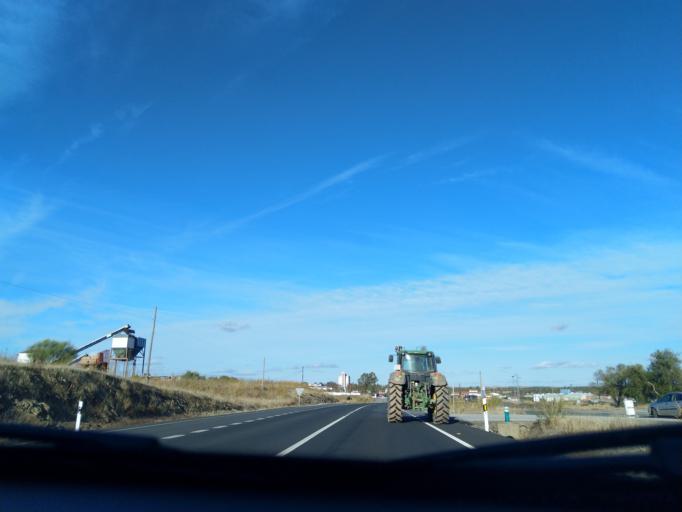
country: ES
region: Extremadura
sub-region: Provincia de Badajoz
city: Ahillones
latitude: 38.2731
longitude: -5.8331
